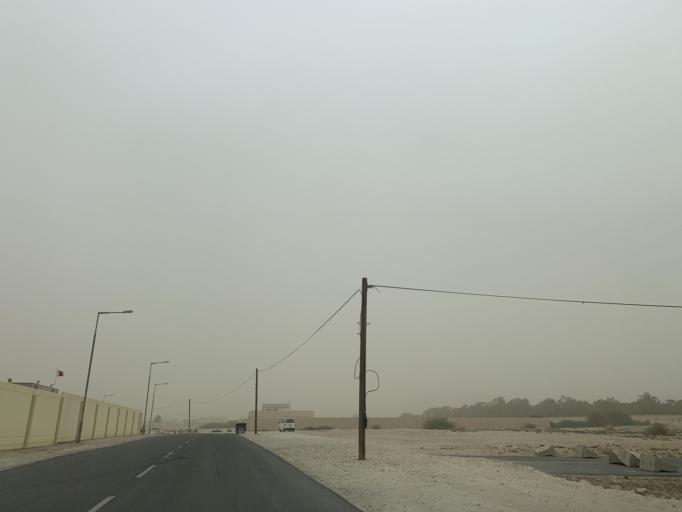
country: BH
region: Central Governorate
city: Madinat Hamad
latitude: 26.1303
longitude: 50.5194
